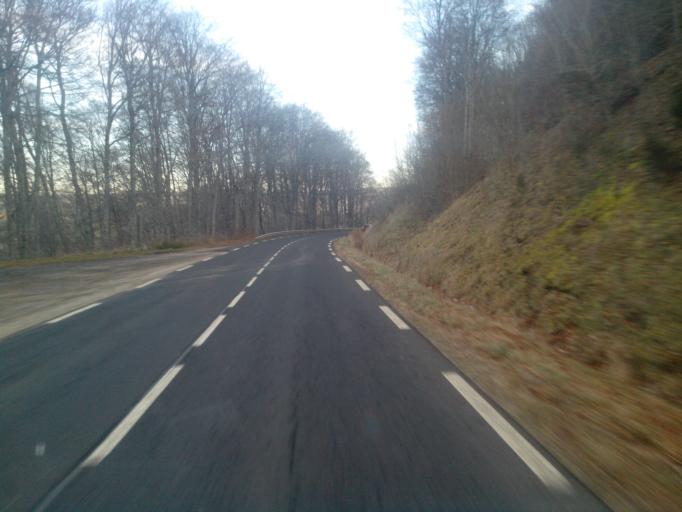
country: FR
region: Auvergne
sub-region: Departement du Cantal
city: Riom-es-Montagnes
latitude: 45.2618
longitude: 2.6897
